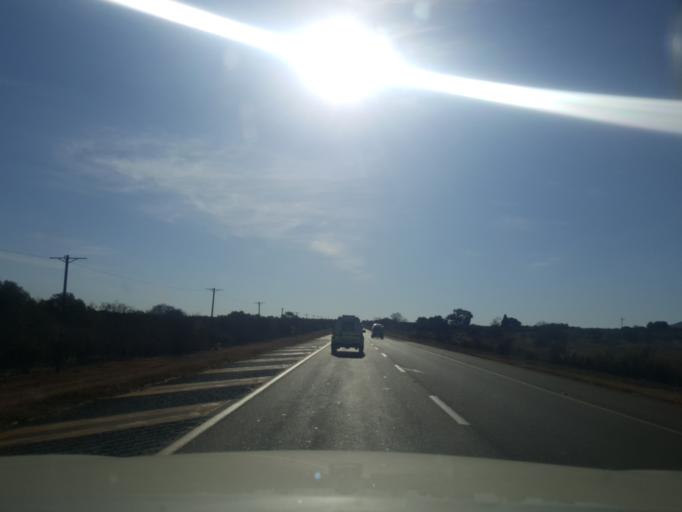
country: ZA
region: North-West
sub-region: Ngaka Modiri Molema District Municipality
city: Zeerust
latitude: -25.5297
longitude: 26.0188
